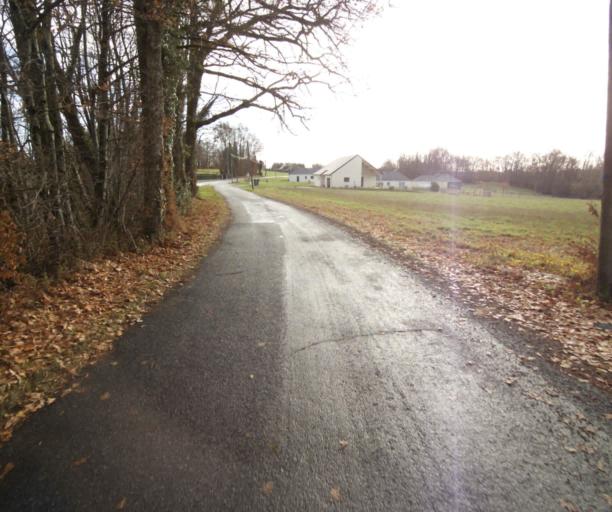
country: FR
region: Limousin
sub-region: Departement de la Correze
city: Saint-Mexant
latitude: 45.2818
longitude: 1.6011
